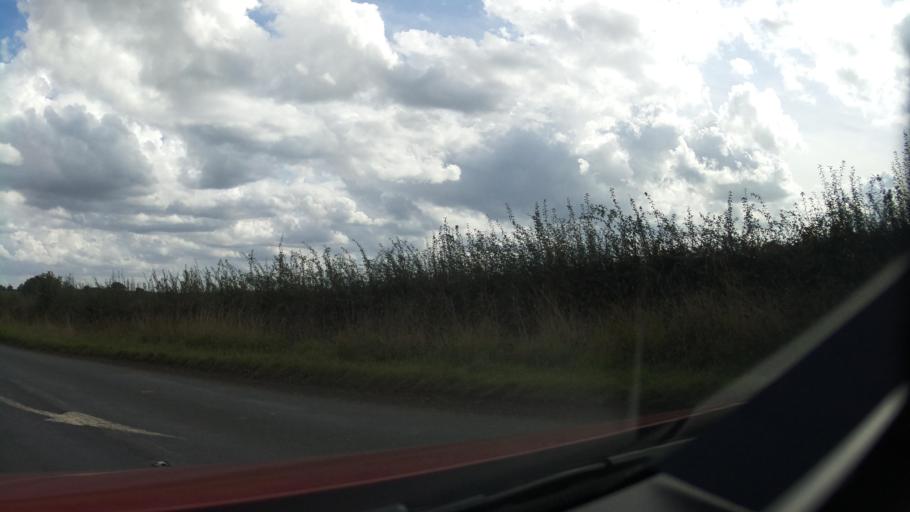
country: GB
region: England
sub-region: North Yorkshire
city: Bedale
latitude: 54.2211
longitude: -1.6368
